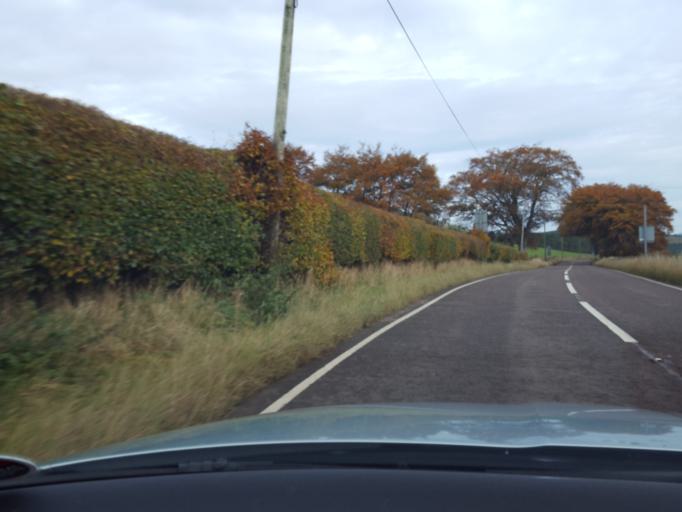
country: GB
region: Scotland
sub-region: South Lanarkshire
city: Biggar
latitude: 55.6784
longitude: -3.4853
